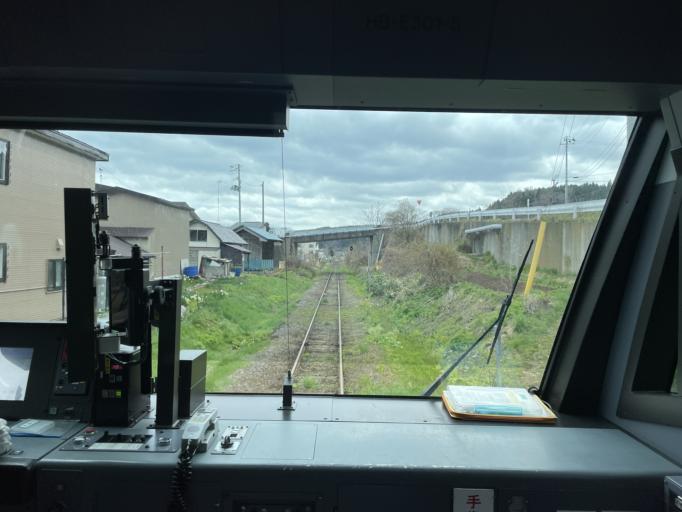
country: JP
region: Aomori
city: Shimokizukuri
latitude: 40.7482
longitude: 140.0916
